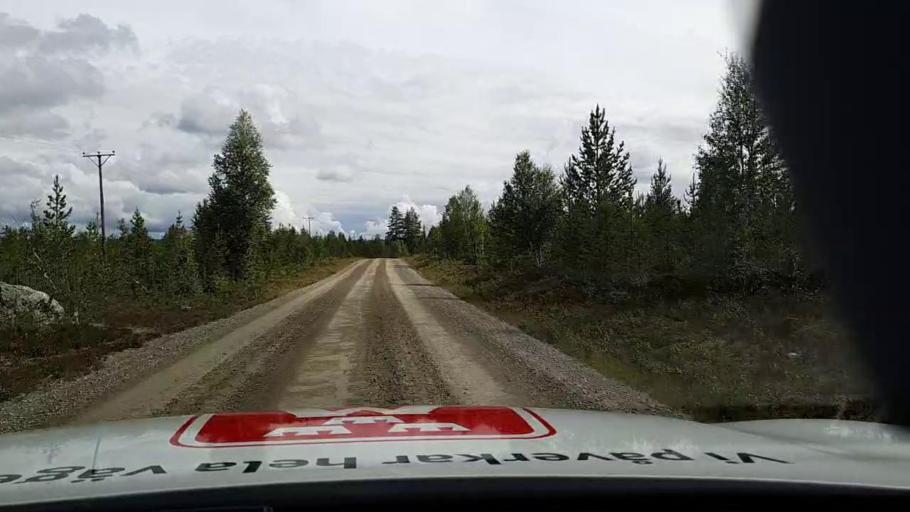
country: SE
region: Jaemtland
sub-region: Are Kommun
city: Jarpen
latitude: 62.5070
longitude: 13.4968
